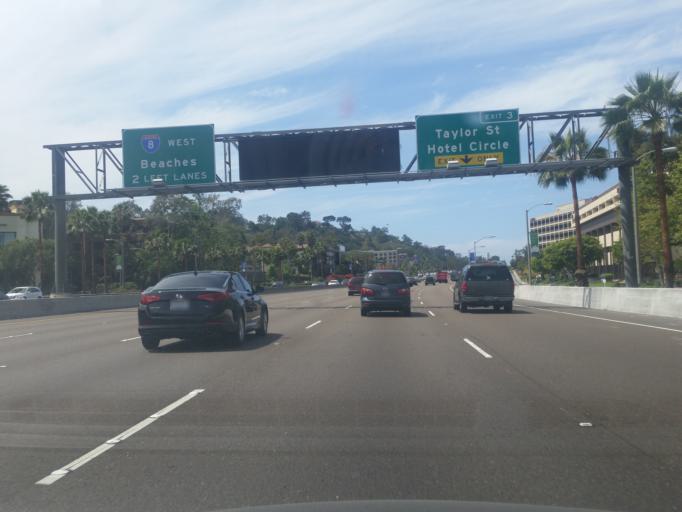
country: US
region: California
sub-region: San Diego County
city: San Diego
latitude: 32.7595
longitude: -117.1756
